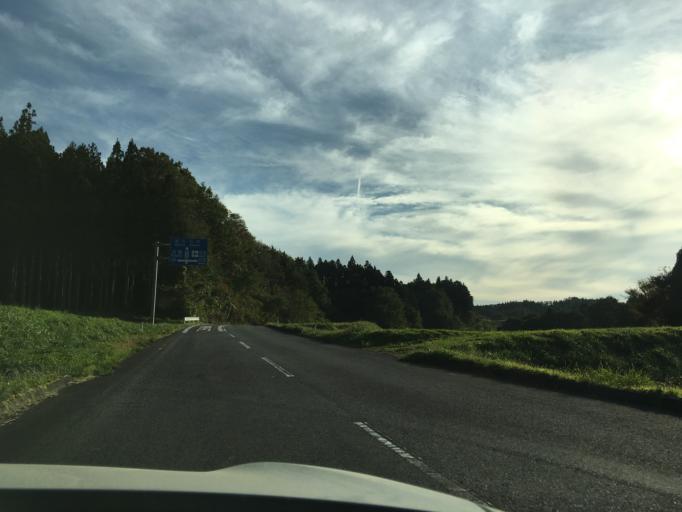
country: JP
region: Fukushima
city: Ishikawa
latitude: 37.1959
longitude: 140.5396
